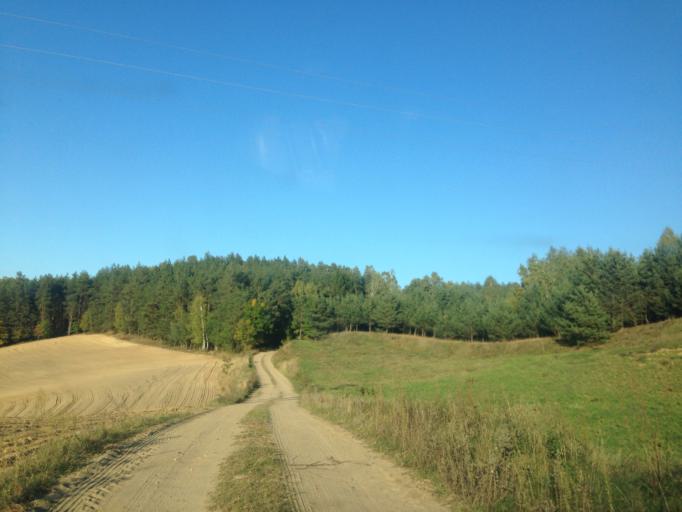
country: PL
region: Kujawsko-Pomorskie
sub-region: Powiat brodnicki
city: Bartniczka
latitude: 53.2718
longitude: 19.6742
